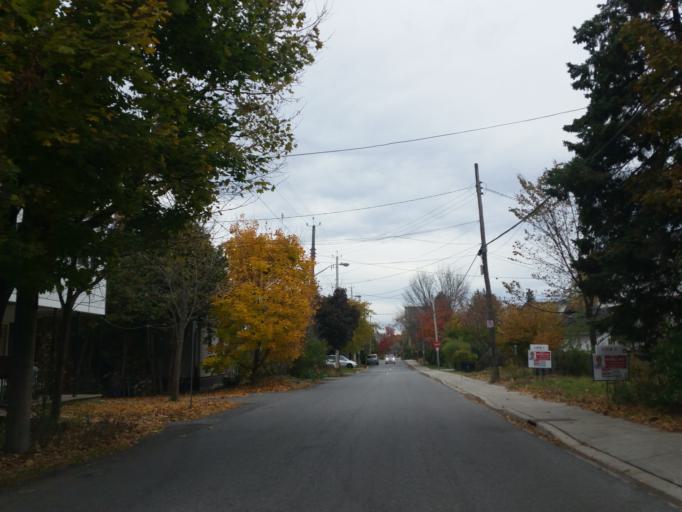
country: CA
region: Ontario
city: Bells Corners
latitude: 45.3697
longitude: -75.7993
